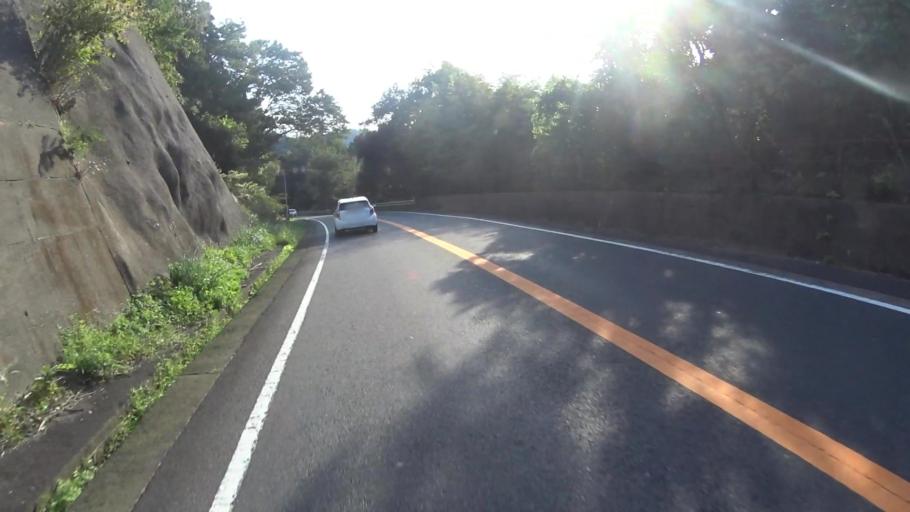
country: JP
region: Hyogo
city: Toyooka
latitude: 35.5929
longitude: 134.8750
